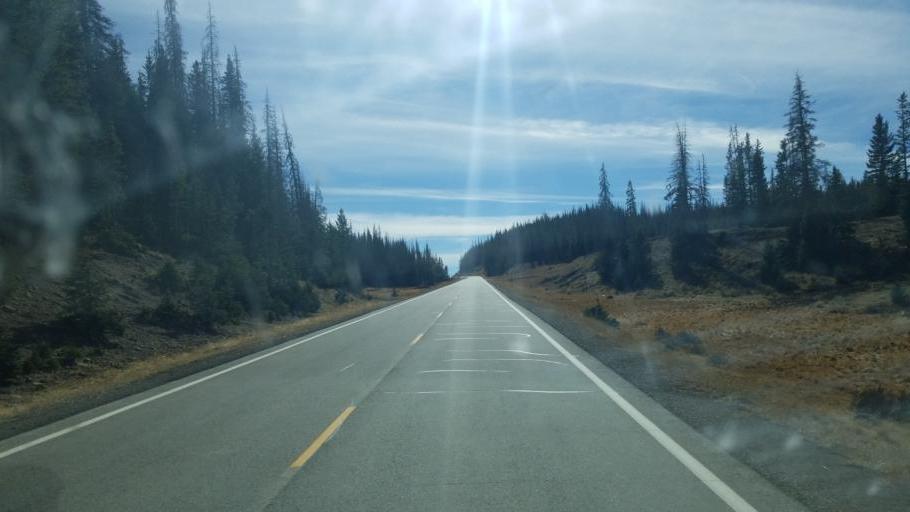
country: US
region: New Mexico
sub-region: Rio Arriba County
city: Chama
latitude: 37.0848
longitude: -106.3813
